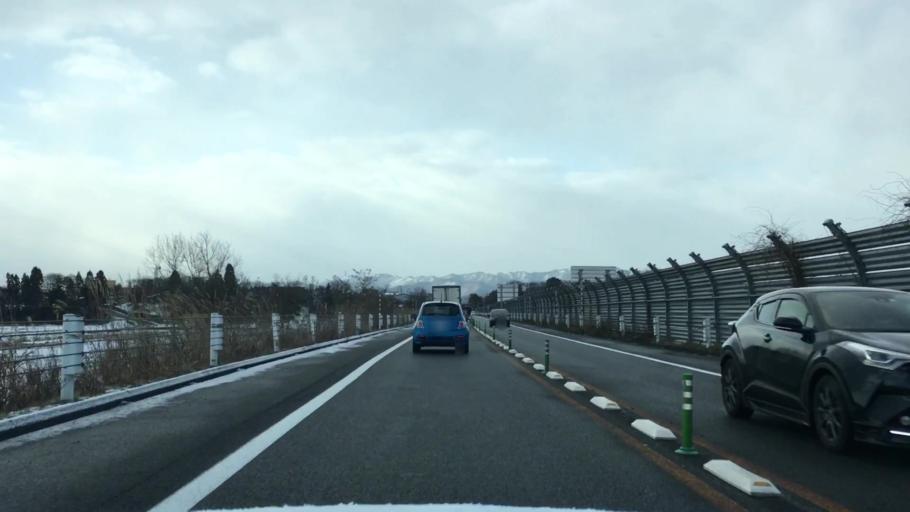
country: JP
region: Akita
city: Odate
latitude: 40.2810
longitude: 140.5390
